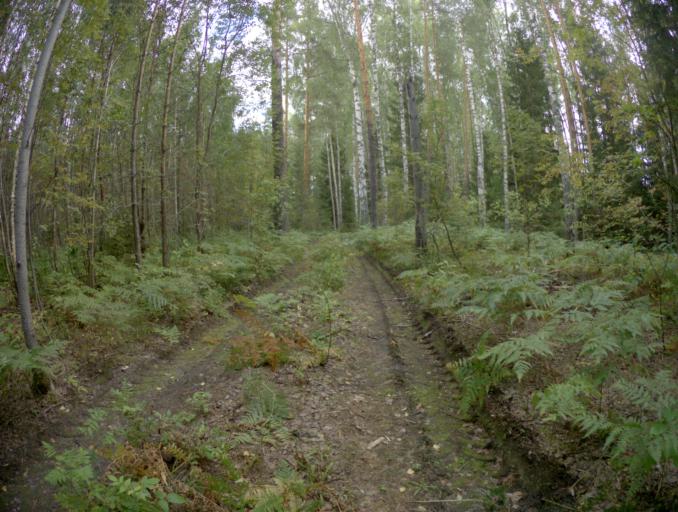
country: RU
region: Vladimir
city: Raduzhnyy
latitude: 55.9656
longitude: 40.2215
